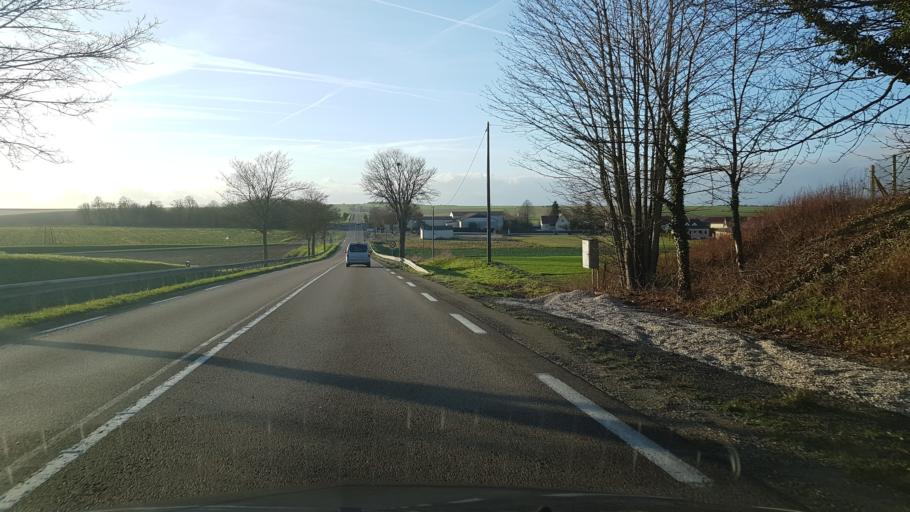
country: FR
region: Champagne-Ardenne
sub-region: Departement de l'Aube
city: Mailly-le-Camp
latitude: 48.7360
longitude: 4.3168
